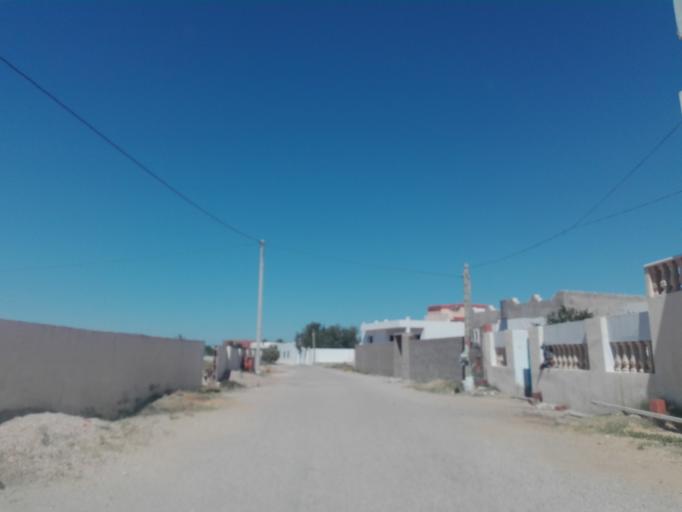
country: TN
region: Safaqis
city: Al Qarmadah
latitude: 34.7128
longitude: 11.1968
